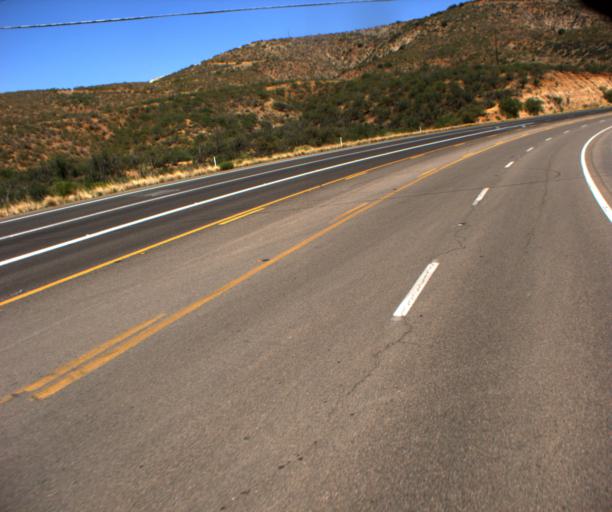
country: US
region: Arizona
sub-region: Gila County
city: Claypool
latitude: 33.4410
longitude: -110.8311
